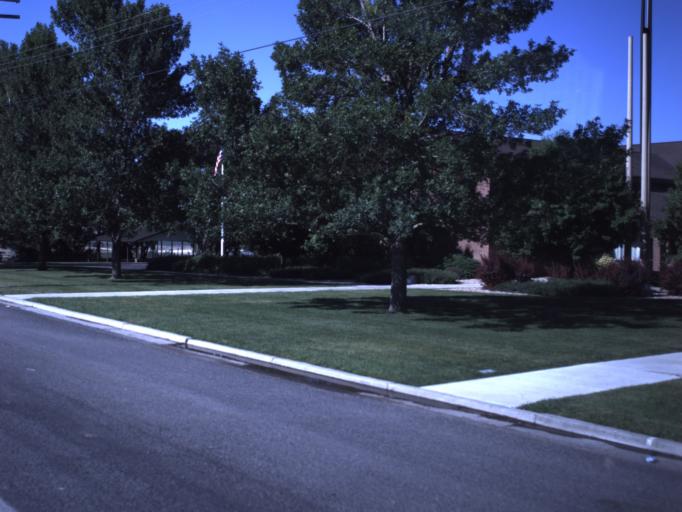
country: US
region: Utah
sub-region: Sanpete County
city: Manti
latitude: 39.1931
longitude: -111.6925
